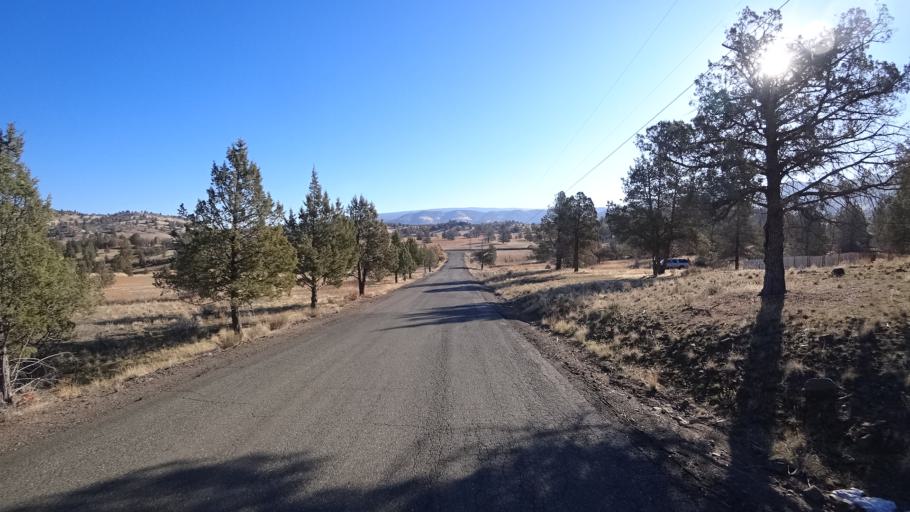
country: US
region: California
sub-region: Siskiyou County
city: Montague
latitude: 41.8888
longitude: -122.4295
